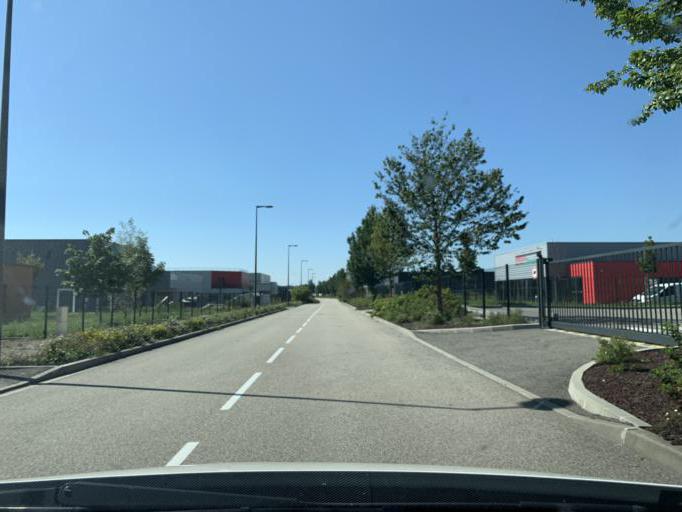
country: FR
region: Rhone-Alpes
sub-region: Departement de l'Ain
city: Chateau-Gaillard
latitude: 45.9787
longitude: 5.3226
